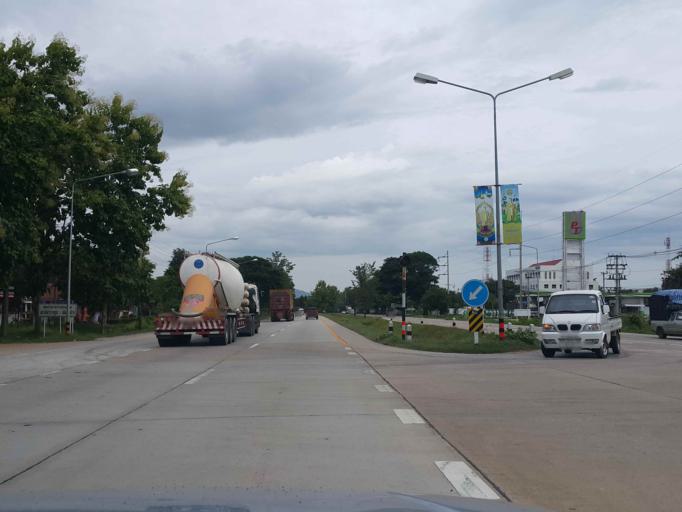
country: TH
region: Lampang
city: Hang Chat
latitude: 18.2970
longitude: 99.4140
